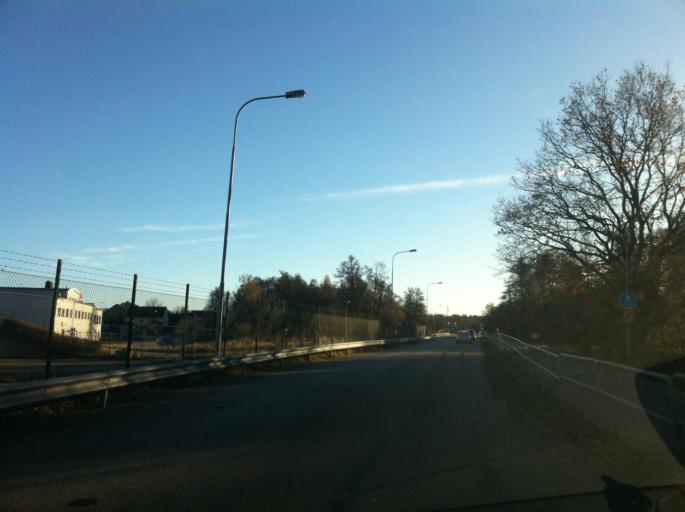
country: SE
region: Blekinge
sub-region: Karlshamns Kommun
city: Karlshamn
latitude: 56.1865
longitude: 14.8475
